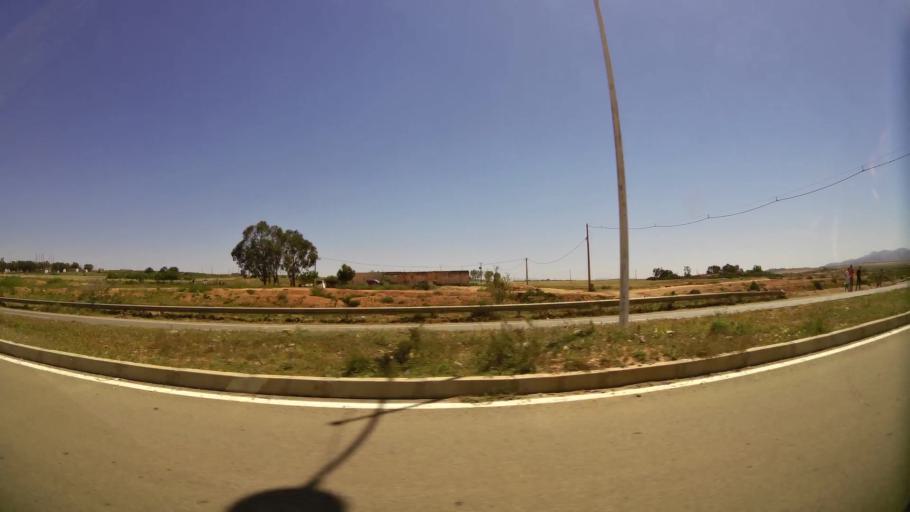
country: MA
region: Oriental
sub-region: Berkane-Taourirt
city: Madagh
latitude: 35.1000
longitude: -2.3324
